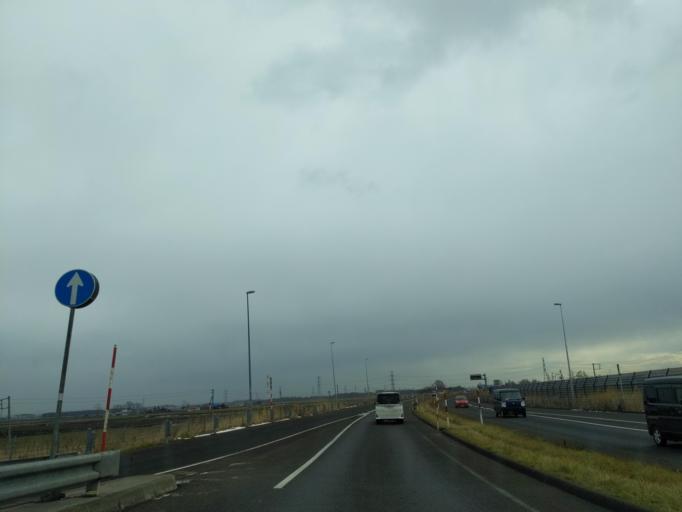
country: JP
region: Hokkaido
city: Tobetsu
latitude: 43.1817
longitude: 141.5601
